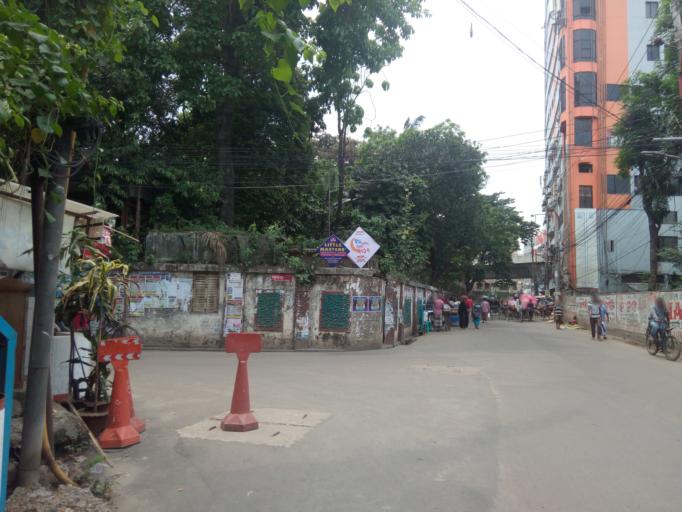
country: BD
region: Dhaka
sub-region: Dhaka
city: Dhaka
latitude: 23.7165
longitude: 90.4196
